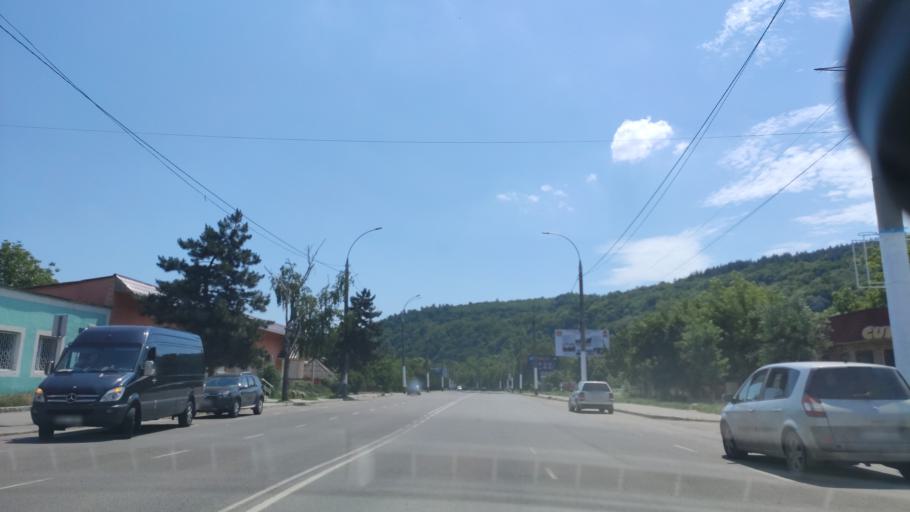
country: MD
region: Raionul Soroca
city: Soroca
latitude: 48.1468
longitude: 28.3021
